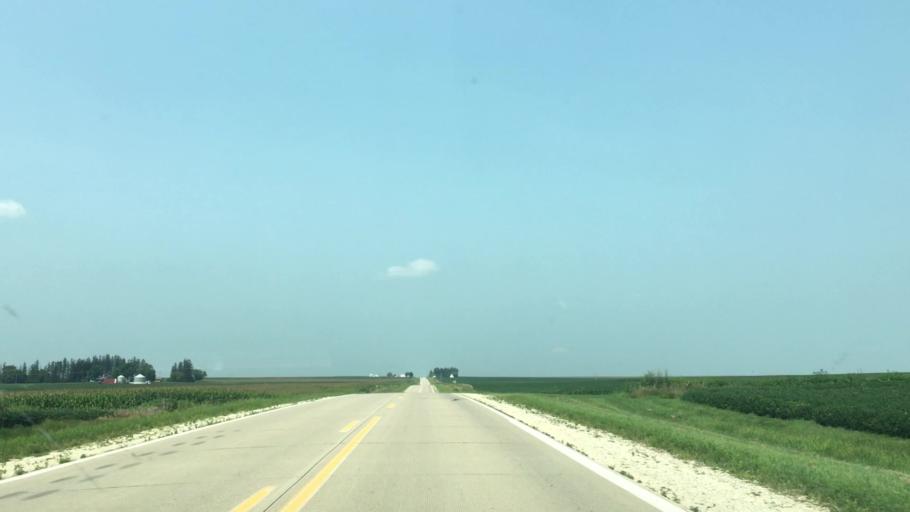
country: US
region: Iowa
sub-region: Fayette County
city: Oelwein
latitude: 42.6943
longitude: -91.8050
